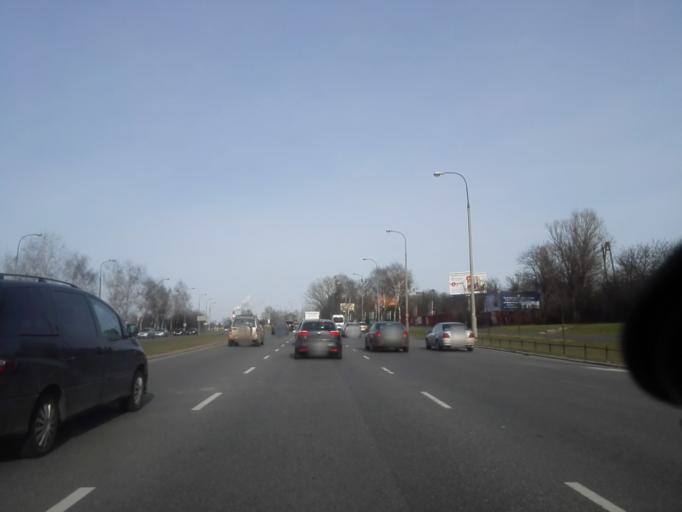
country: PL
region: Masovian Voivodeship
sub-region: Warszawa
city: Ursynow
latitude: 52.1672
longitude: 21.0342
